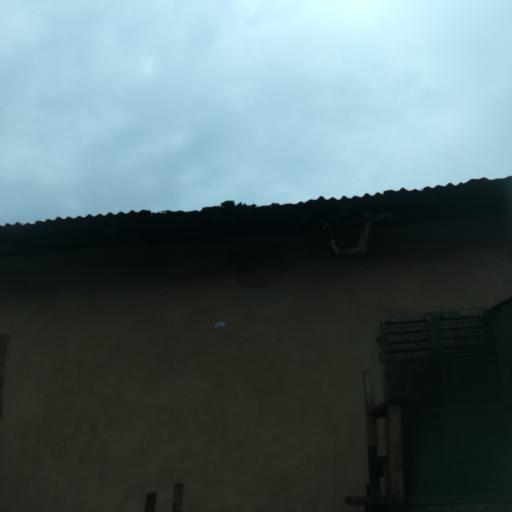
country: NG
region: Lagos
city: Oshodi
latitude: 6.5565
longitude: 3.3438
